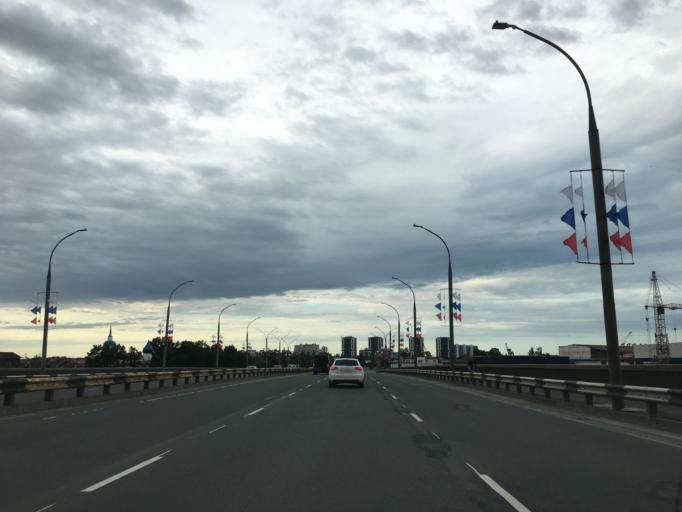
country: RU
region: Pskov
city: Pskov
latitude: 57.8257
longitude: 28.2928
